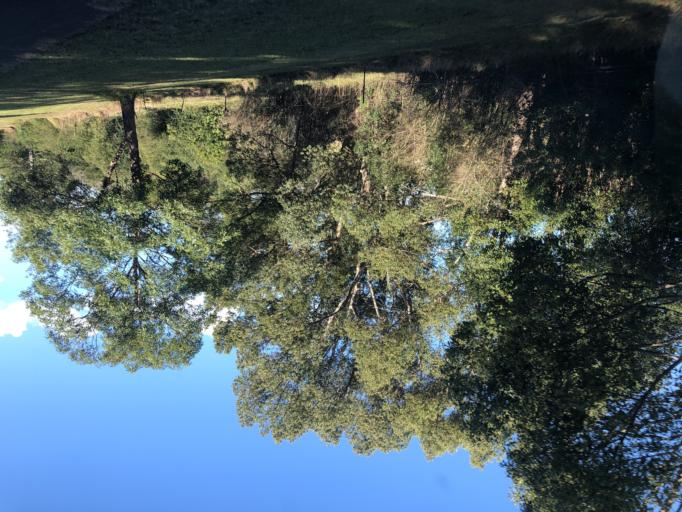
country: AU
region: New South Wales
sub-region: Nambucca Shire
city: Bowraville
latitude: -30.6495
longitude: 152.8574
